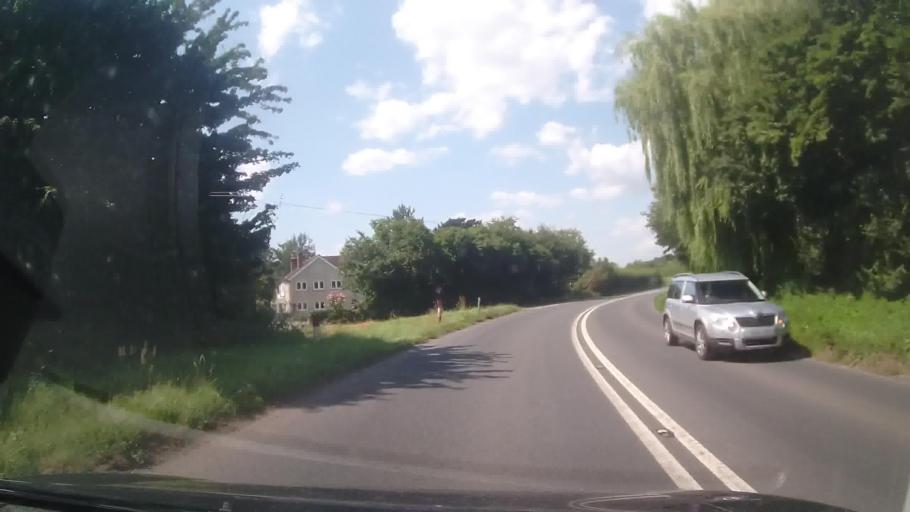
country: GB
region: England
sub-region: Herefordshire
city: Bodenham
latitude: 52.1490
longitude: -2.6440
